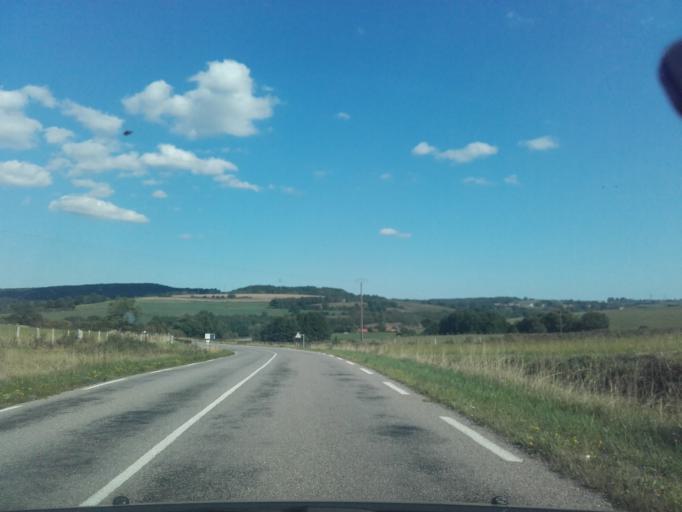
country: FR
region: Bourgogne
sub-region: Departement de Saone-et-Loire
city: Epinac
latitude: 46.9714
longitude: 4.5179
